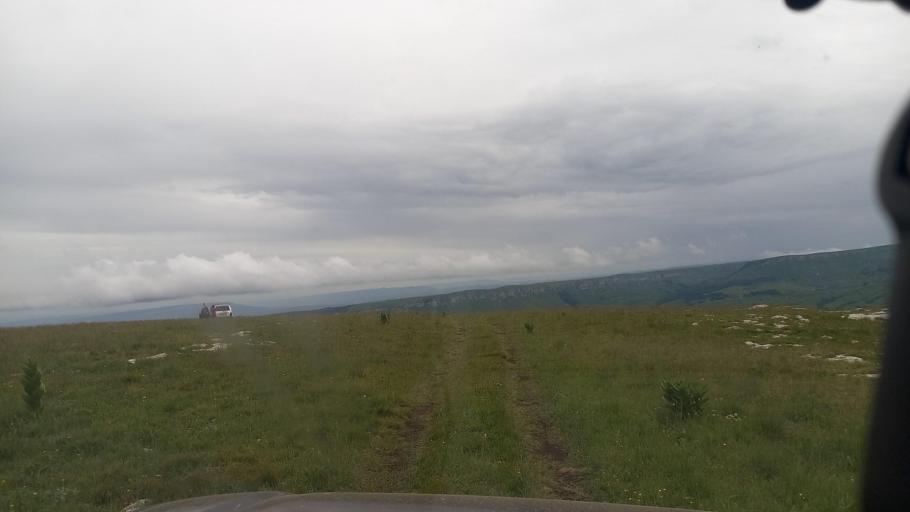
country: RU
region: Karachayevo-Cherkesiya
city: Pregradnaya
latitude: 43.9740
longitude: 41.2940
